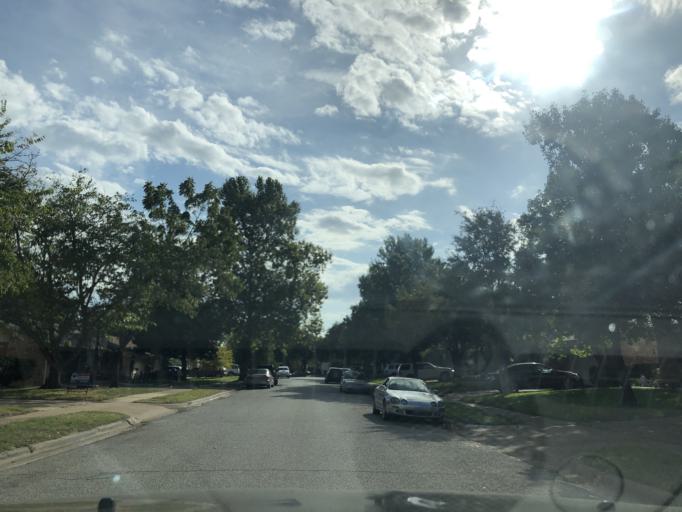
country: US
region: Texas
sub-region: Dallas County
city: Garland
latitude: 32.8844
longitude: -96.6628
